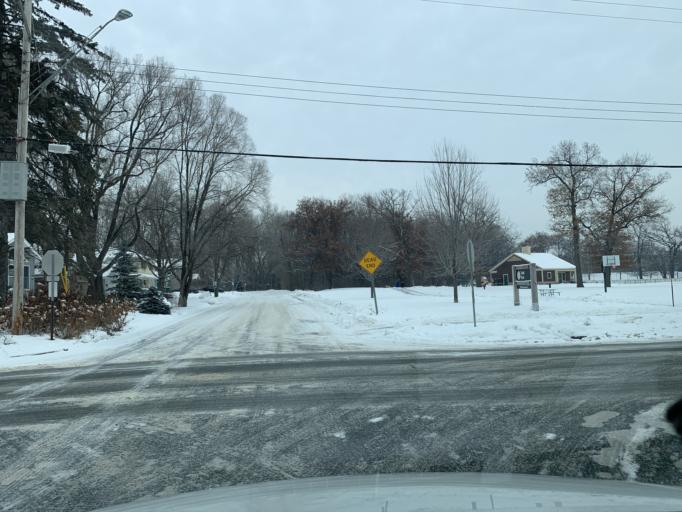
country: US
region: Minnesota
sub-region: Hennepin County
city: Edina
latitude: 44.9168
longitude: -93.3581
